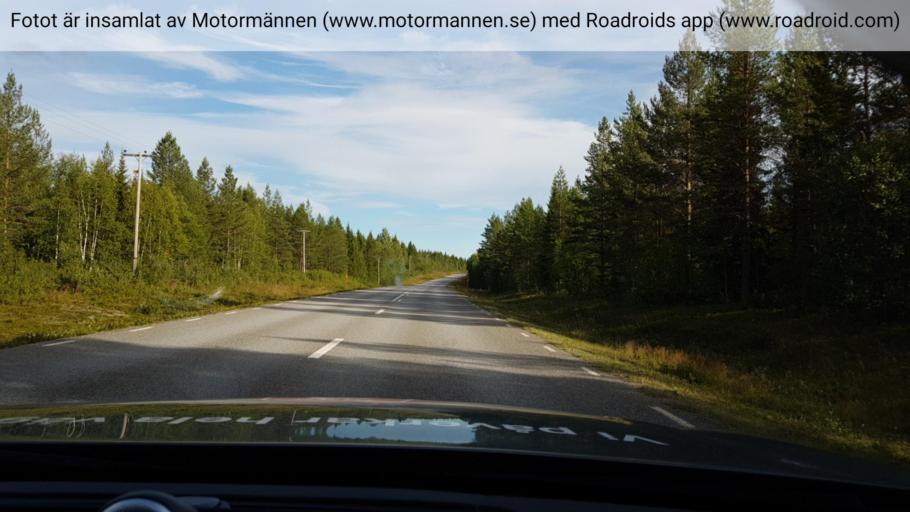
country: SE
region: Jaemtland
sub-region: Stroemsunds Kommun
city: Stroemsund
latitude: 64.2780
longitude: 15.3705
